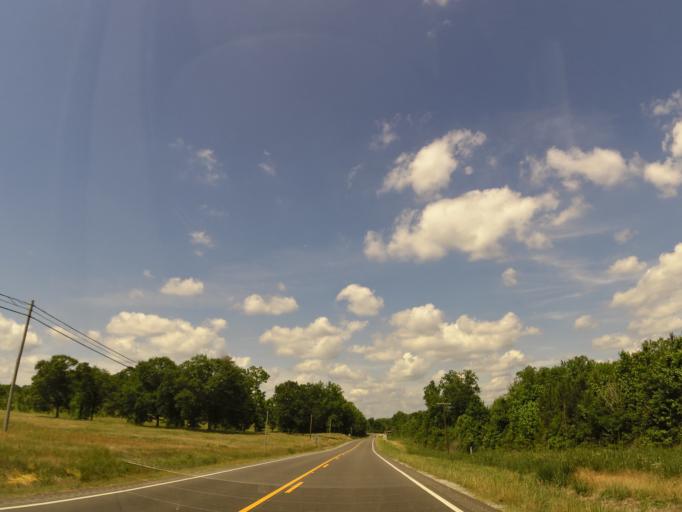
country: US
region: Alabama
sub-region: Lamar County
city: Sulligent
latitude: 33.9216
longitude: -88.0402
